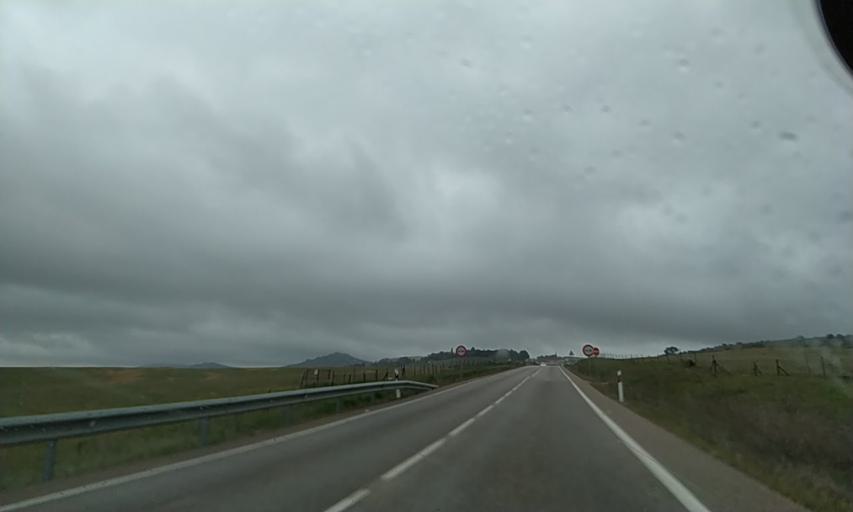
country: ES
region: Extremadura
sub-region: Provincia de Caceres
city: Caceres
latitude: 39.4967
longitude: -6.3867
